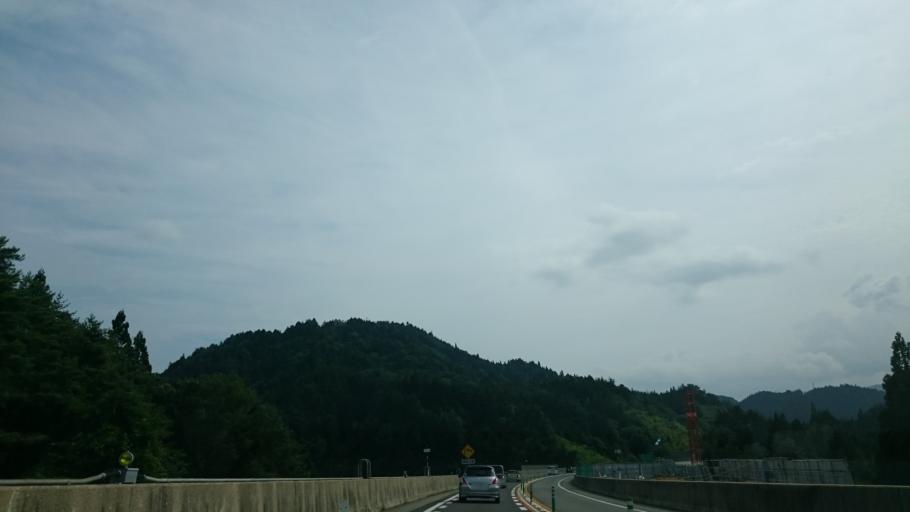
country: JP
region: Gifu
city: Gujo
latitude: 35.9304
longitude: 136.8789
